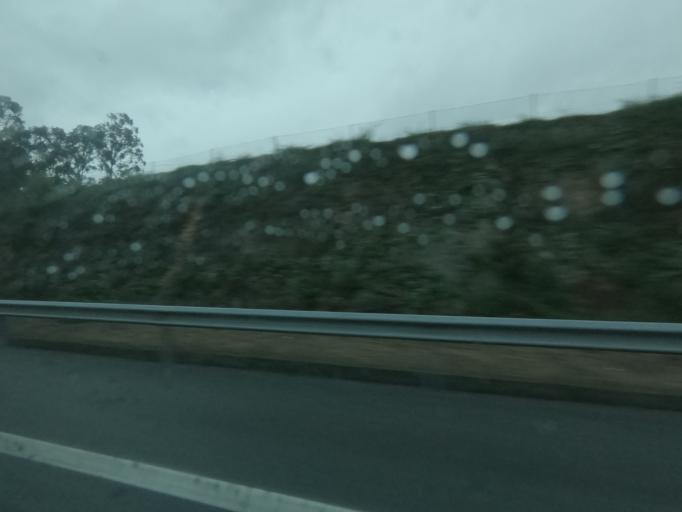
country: ES
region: Galicia
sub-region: Provincia de Pontevedra
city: Pontevedra
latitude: 42.3819
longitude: -8.6377
